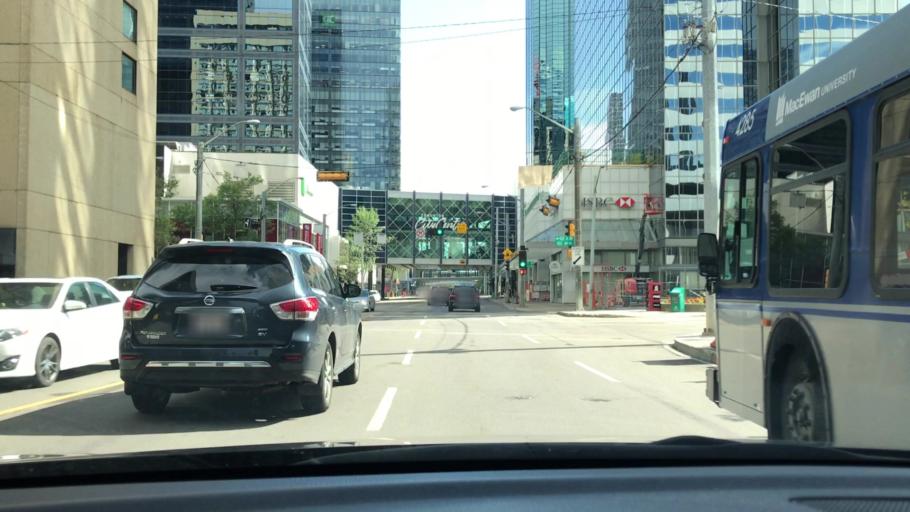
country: CA
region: Alberta
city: Edmonton
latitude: 53.5455
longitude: -113.4938
